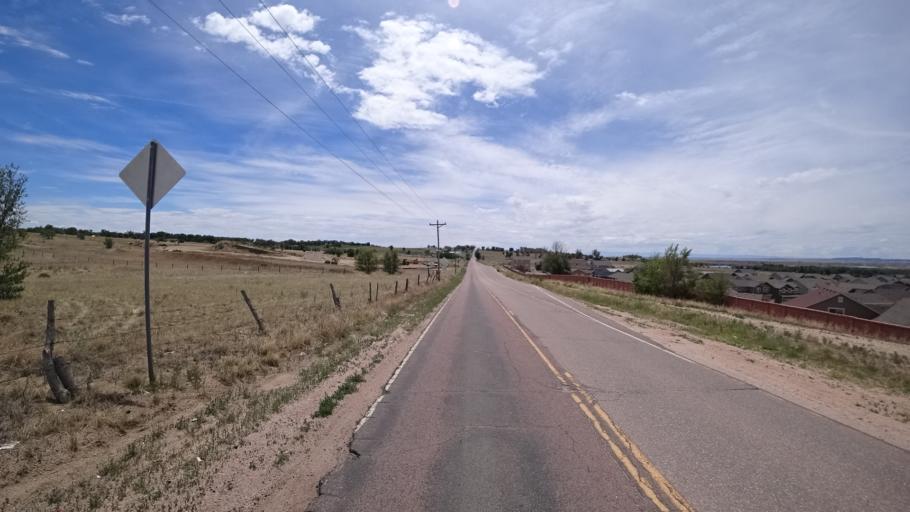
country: US
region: Colorado
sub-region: El Paso County
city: Fountain
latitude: 38.6926
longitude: -104.6737
